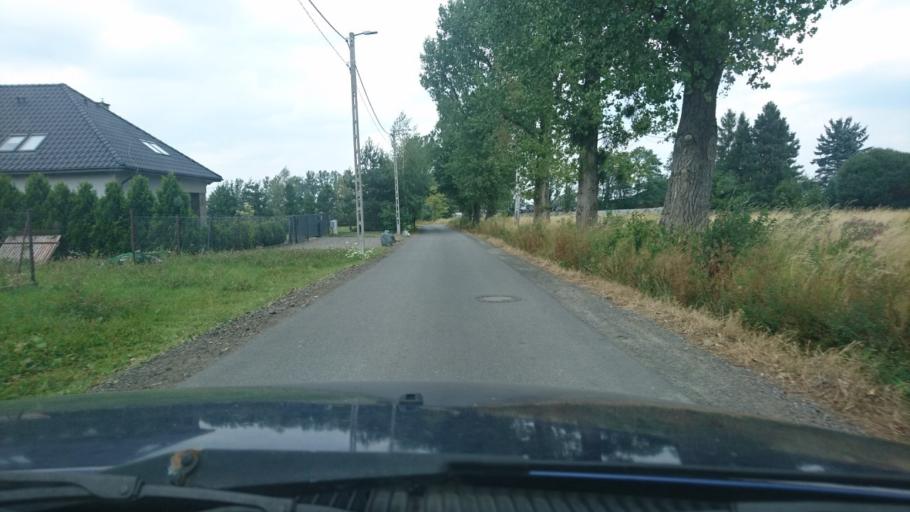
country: PL
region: Silesian Voivodeship
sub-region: Powiat bielski
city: Jaworze
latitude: 49.8051
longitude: 18.9746
